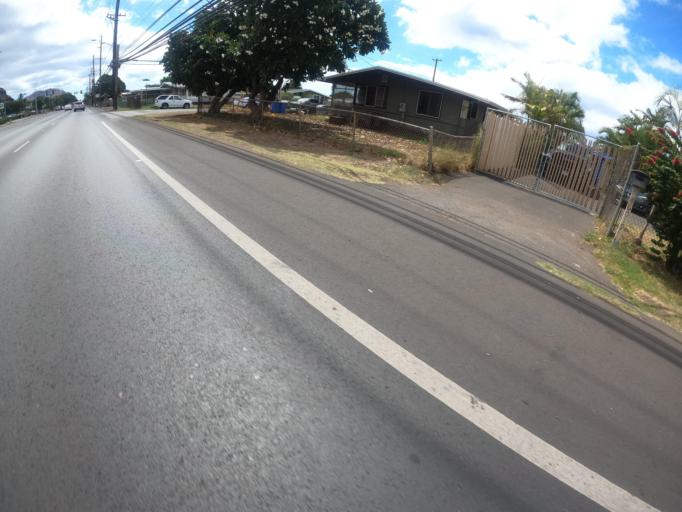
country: US
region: Hawaii
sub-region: Honolulu County
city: Waianae
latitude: 21.4405
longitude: -158.1865
